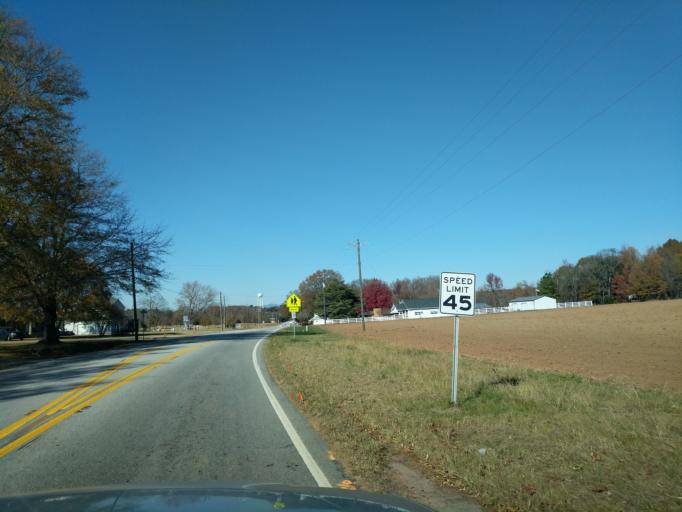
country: US
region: South Carolina
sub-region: Spartanburg County
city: Duncan
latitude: 34.9751
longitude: -82.1581
